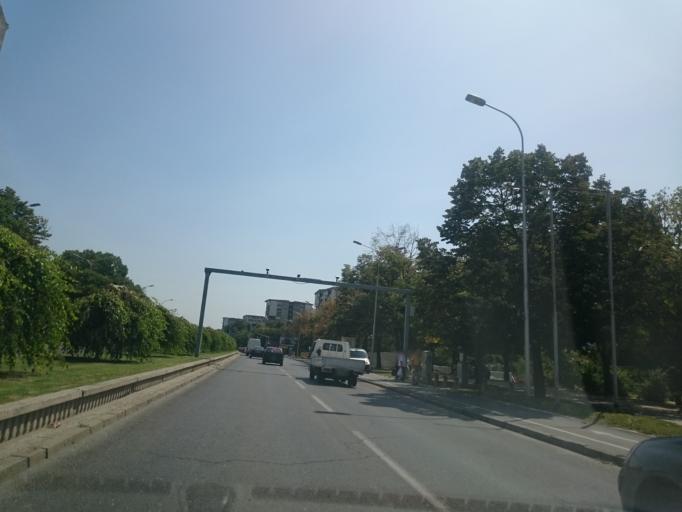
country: MK
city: Krushopek
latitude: 42.0054
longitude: 21.3805
